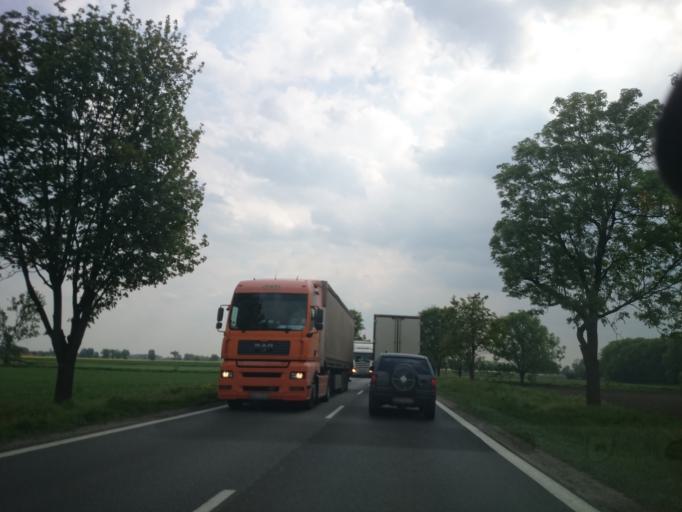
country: PL
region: Lower Silesian Voivodeship
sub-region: Powiat wroclawski
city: Kobierzyce
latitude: 50.9785
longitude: 16.9468
